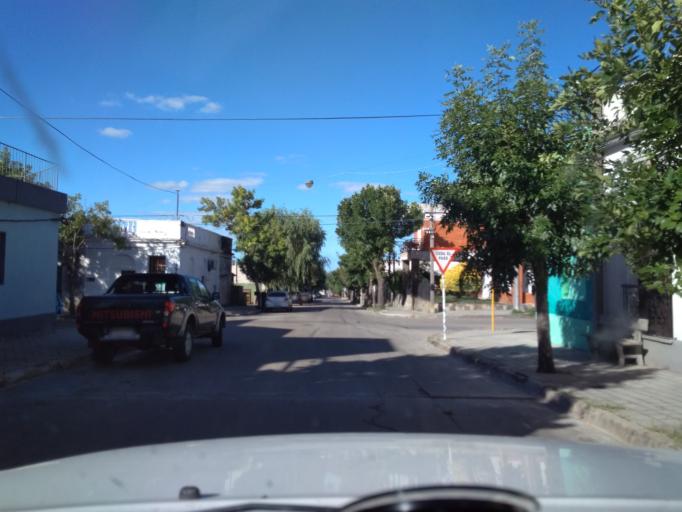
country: UY
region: Florida
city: Florida
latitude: -34.0953
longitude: -56.2150
